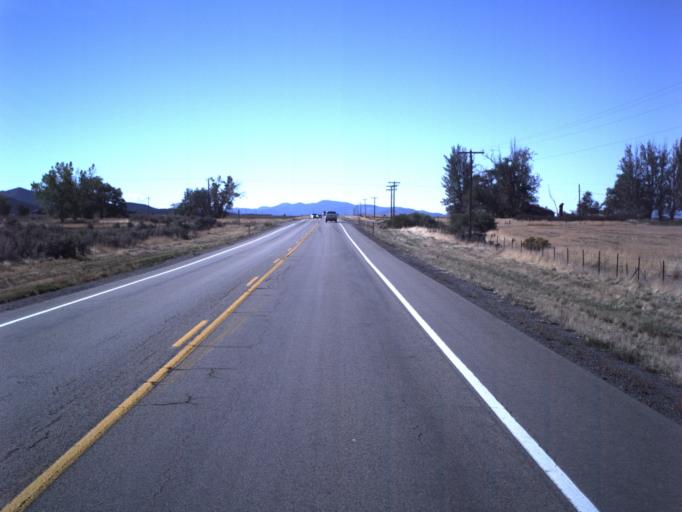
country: US
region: Utah
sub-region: Juab County
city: Nephi
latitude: 39.4788
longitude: -111.8907
